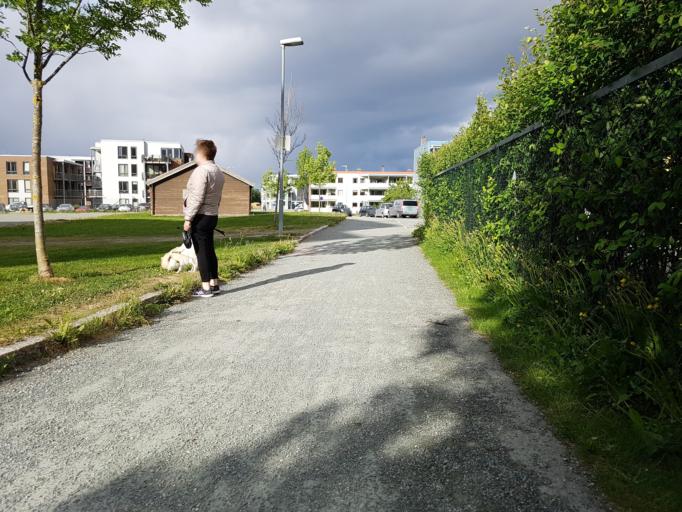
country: NO
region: Sor-Trondelag
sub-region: Trondheim
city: Trondheim
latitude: 63.4308
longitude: 10.4464
